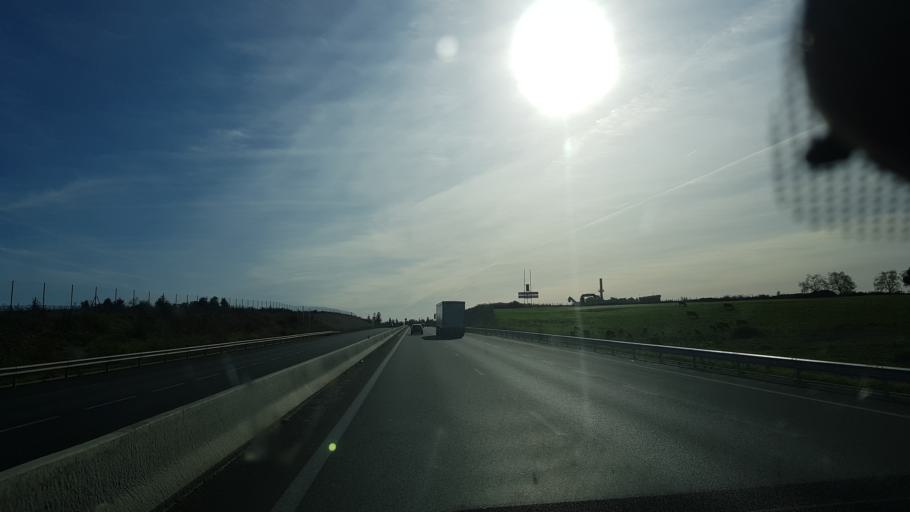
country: FR
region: Poitou-Charentes
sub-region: Departement de la Charente
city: Baignes-Sainte-Radegonde
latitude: 45.3556
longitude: -0.1966
